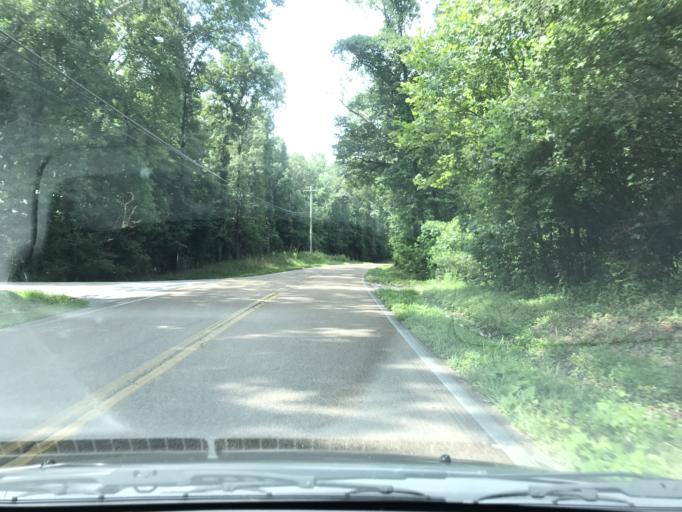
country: US
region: Tennessee
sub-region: Hamilton County
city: Lakesite
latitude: 35.1813
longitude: -85.1123
